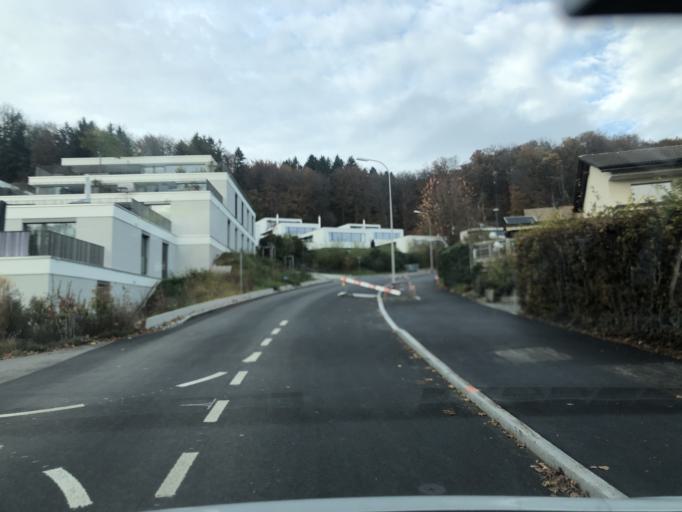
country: CH
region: Aargau
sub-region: Bezirk Baden
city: Birmenstorf
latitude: 47.4608
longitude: 8.2780
